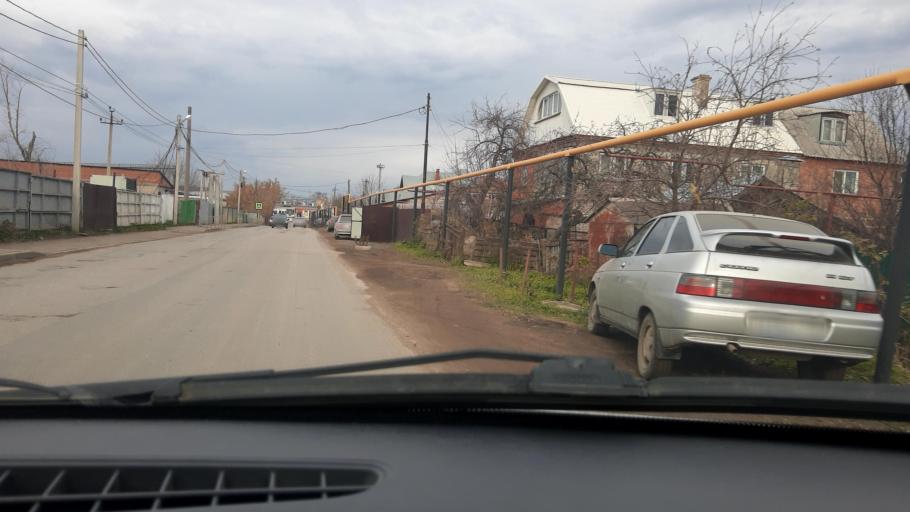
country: RU
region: Bashkortostan
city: Mikhaylovka
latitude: 54.6979
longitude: 55.8494
